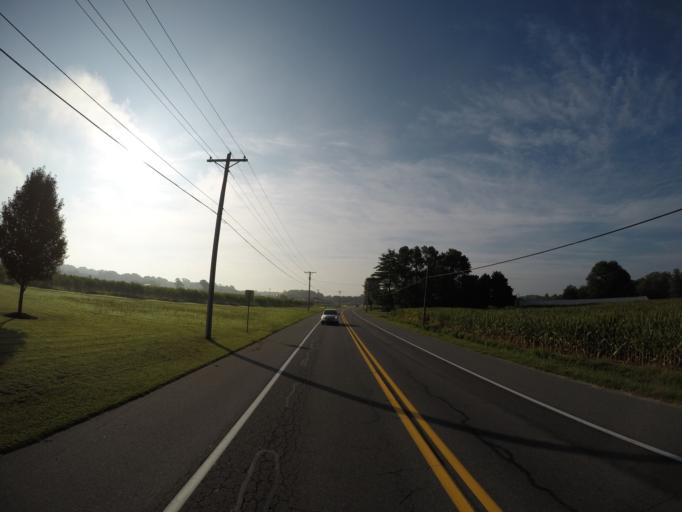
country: US
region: Delaware
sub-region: Sussex County
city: Selbyville
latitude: 38.5419
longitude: -75.2231
